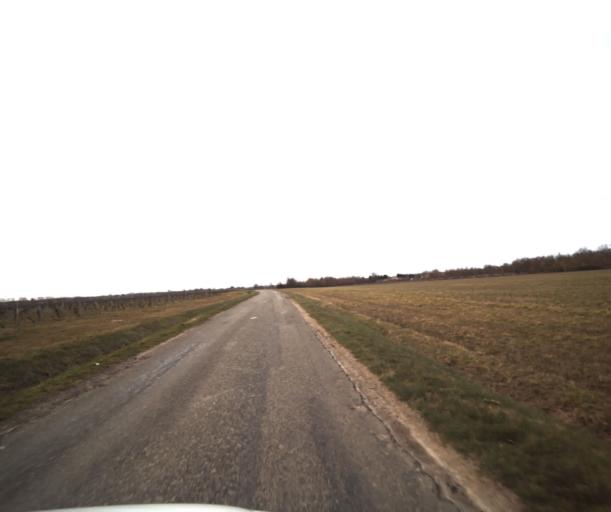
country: FR
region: Midi-Pyrenees
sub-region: Departement du Tarn-et-Garonne
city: Campsas
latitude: 43.8976
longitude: 1.3443
